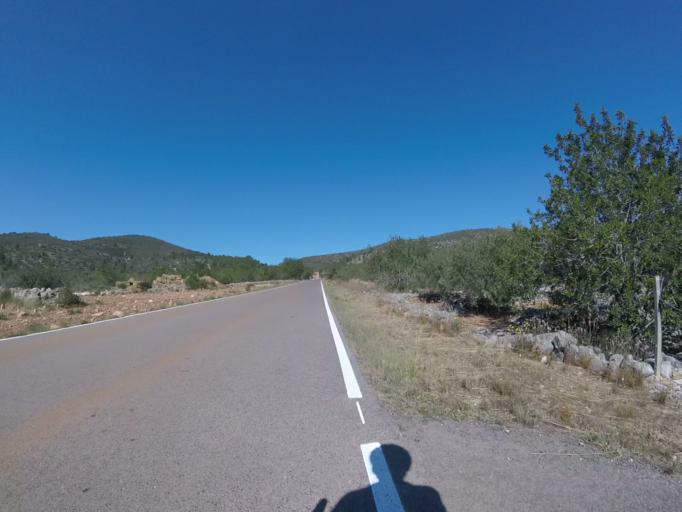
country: ES
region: Valencia
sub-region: Provincia de Castello
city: Santa Magdalena de Pulpis
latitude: 40.3811
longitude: 0.2641
